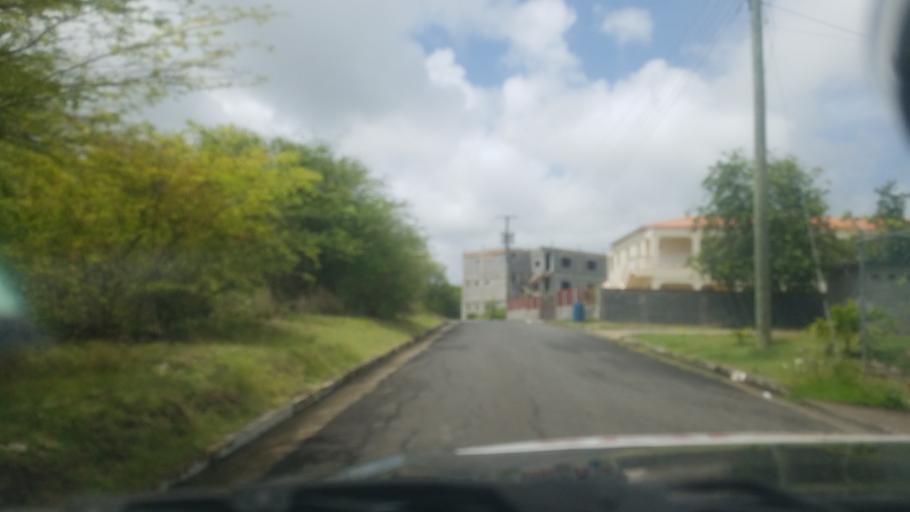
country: LC
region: Laborie Quarter
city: Laborie
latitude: 13.7466
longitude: -60.9713
